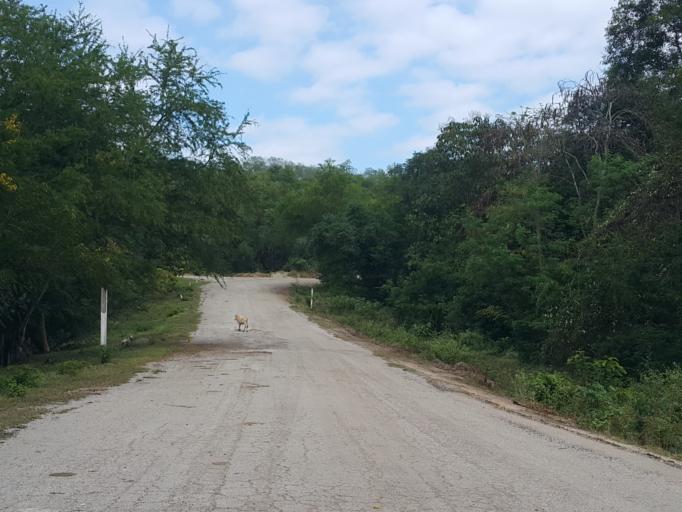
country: TH
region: Lampang
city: Mae Mo
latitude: 18.3257
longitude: 99.7516
